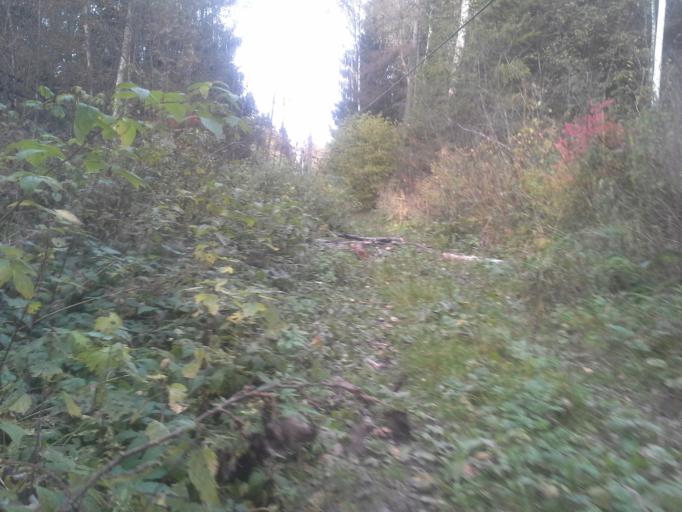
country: RU
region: Moskovskaya
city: Selyatino
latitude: 55.4570
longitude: 36.9739
